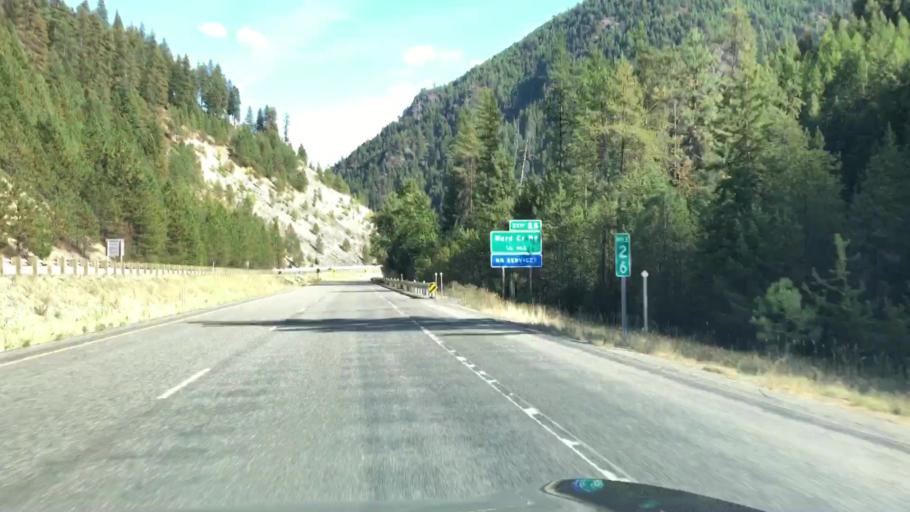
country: US
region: Montana
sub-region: Sanders County
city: Thompson Falls
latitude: 47.3156
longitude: -115.2402
